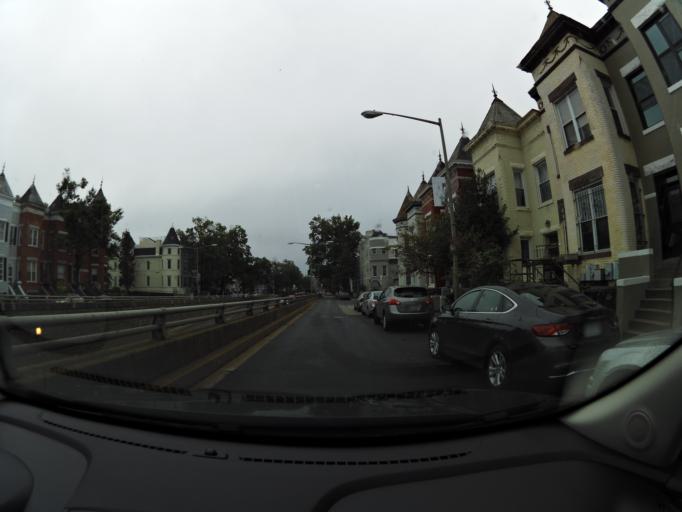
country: US
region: Washington, D.C.
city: Washington, D.C.
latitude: 38.9153
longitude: -77.0092
